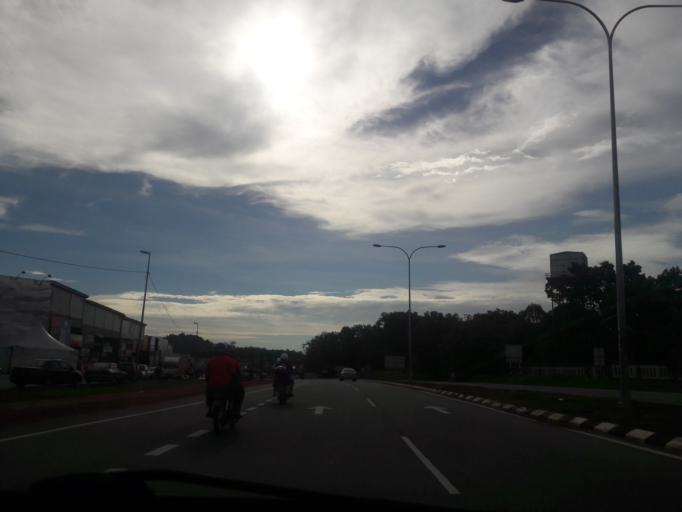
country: MY
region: Kedah
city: Sungai Petani
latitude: 5.6252
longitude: 100.5326
